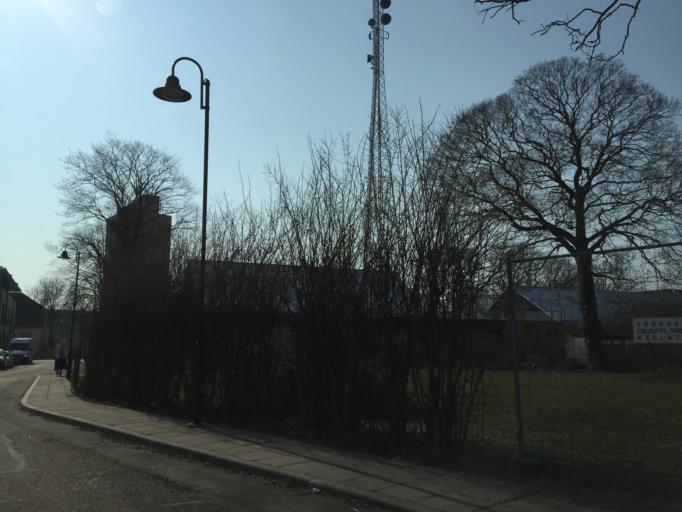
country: EE
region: Saare
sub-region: Kuressaare linn
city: Kuressaare
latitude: 58.2553
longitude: 22.4890
